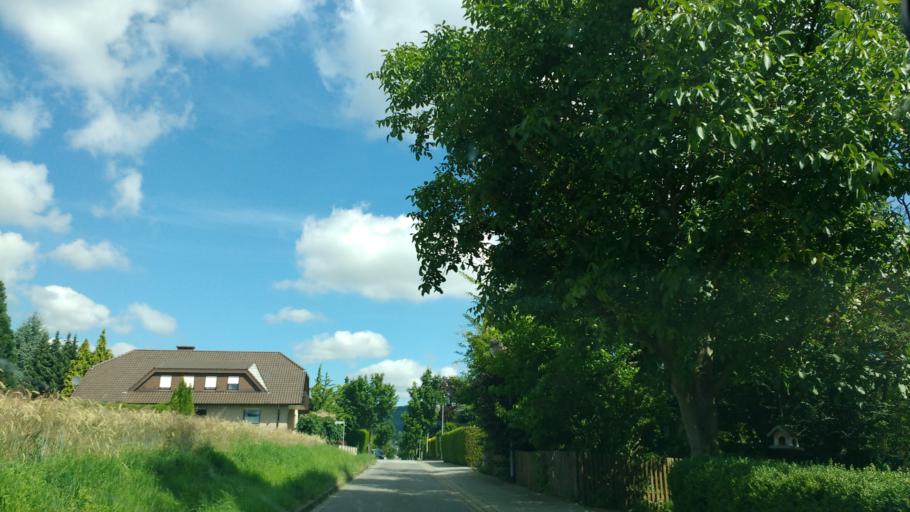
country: DE
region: Lower Saxony
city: Bad Pyrmont
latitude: 51.9788
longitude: 9.2276
